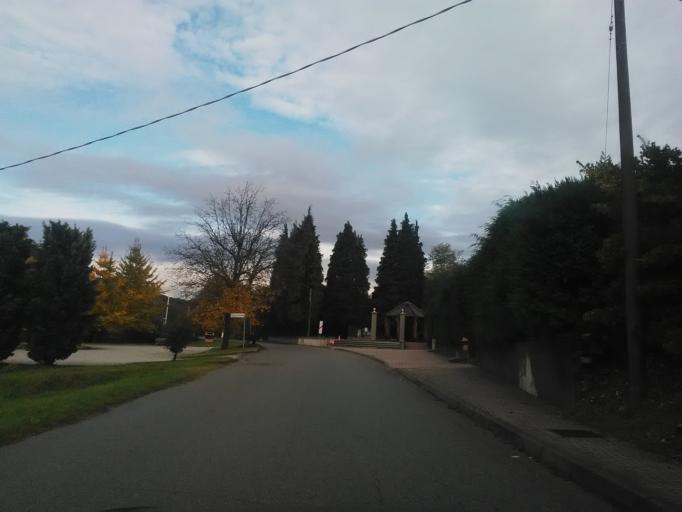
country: IT
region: Piedmont
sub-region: Provincia di Novara
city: Prato Sesia
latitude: 45.6478
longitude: 8.3706
